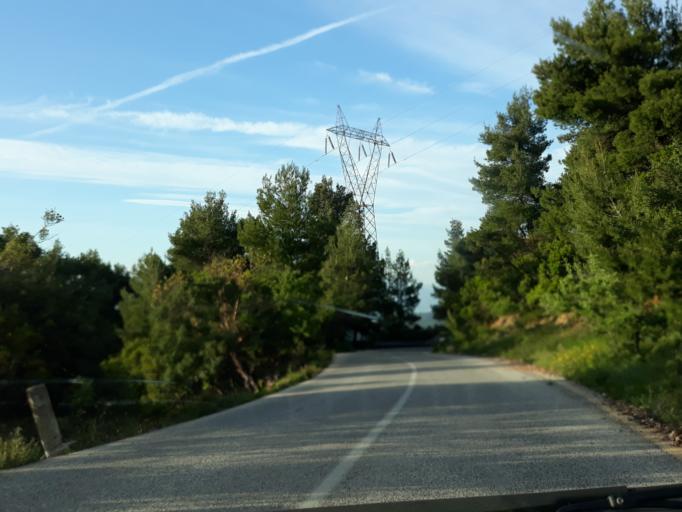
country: GR
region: Attica
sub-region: Nomarchia Anatolikis Attikis
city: Afidnes
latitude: 38.2242
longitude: 23.7890
